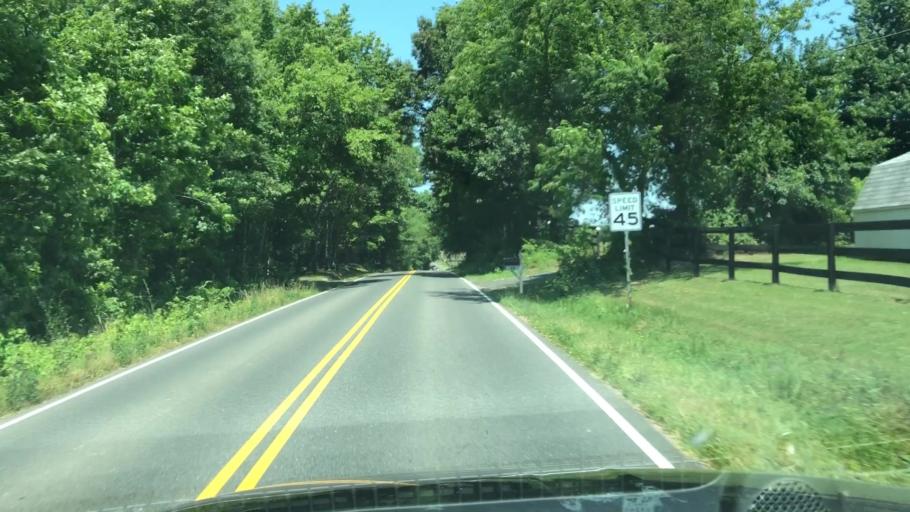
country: US
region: Virginia
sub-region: Stafford County
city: Falmouth
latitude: 38.4032
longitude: -77.5655
